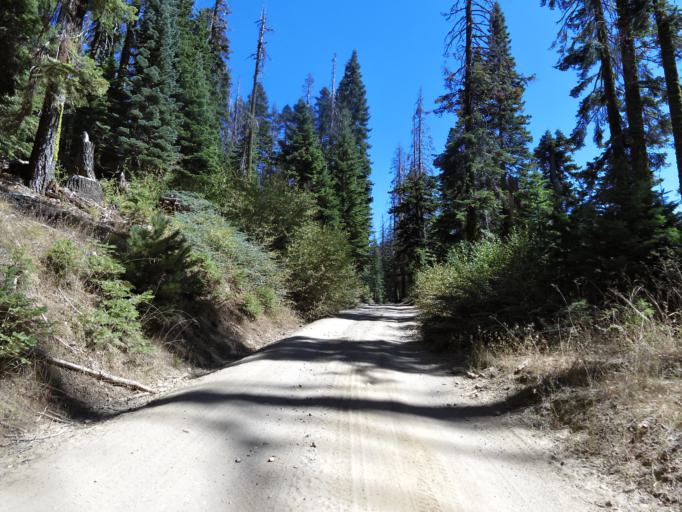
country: US
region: California
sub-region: Madera County
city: Oakhurst
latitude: 37.4372
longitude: -119.5131
